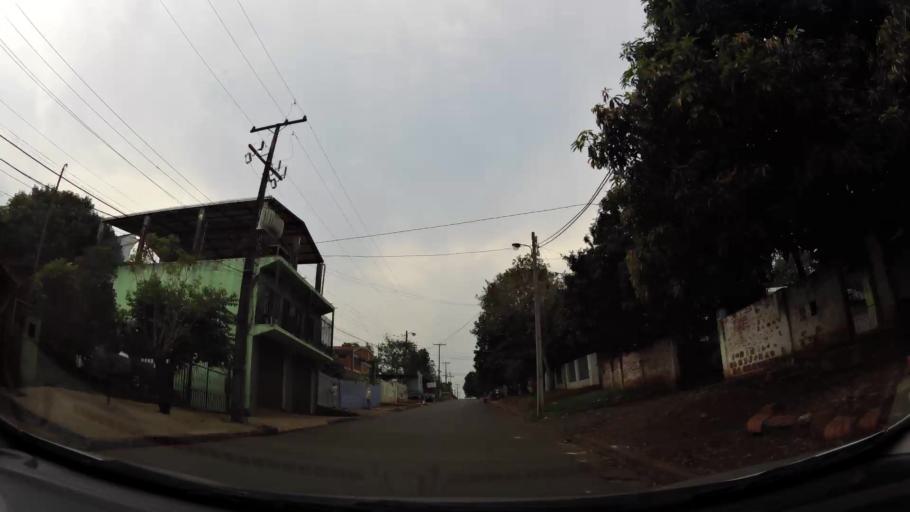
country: PY
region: Alto Parana
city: Presidente Franco
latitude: -25.5382
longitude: -54.6135
